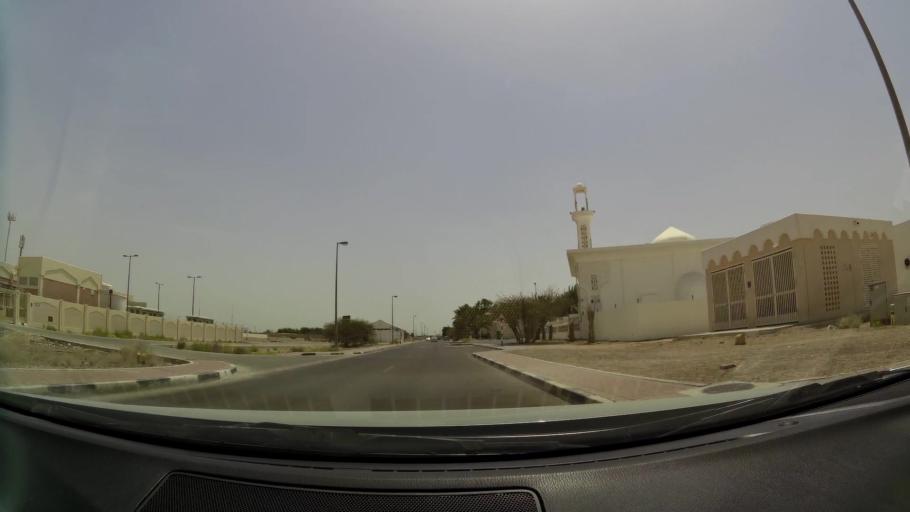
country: AE
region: Abu Dhabi
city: Al Ain
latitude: 24.1862
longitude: 55.7188
